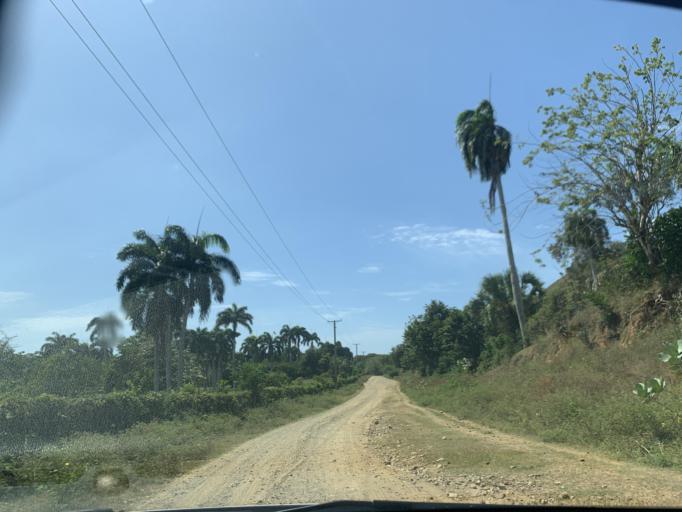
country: DO
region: Puerto Plata
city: Luperon
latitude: 19.8836
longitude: -70.8720
